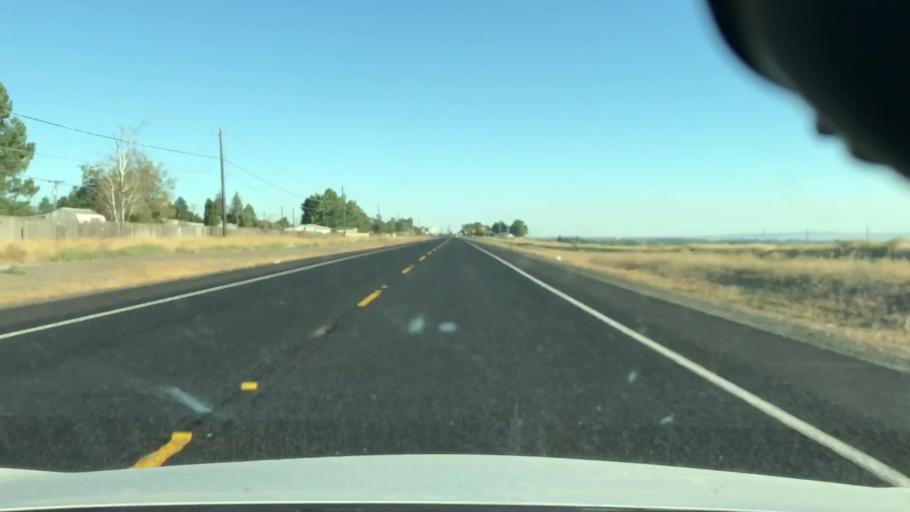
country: US
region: Washington
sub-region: Grant County
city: Moses Lake North
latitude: 47.1692
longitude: -119.3279
